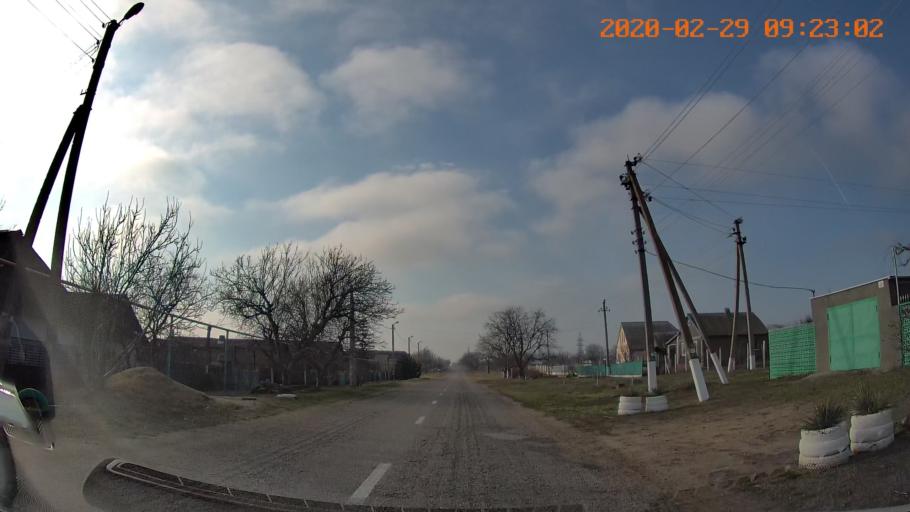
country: MD
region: Telenesti
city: Pervomaisc
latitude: 46.7300
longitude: 29.9625
